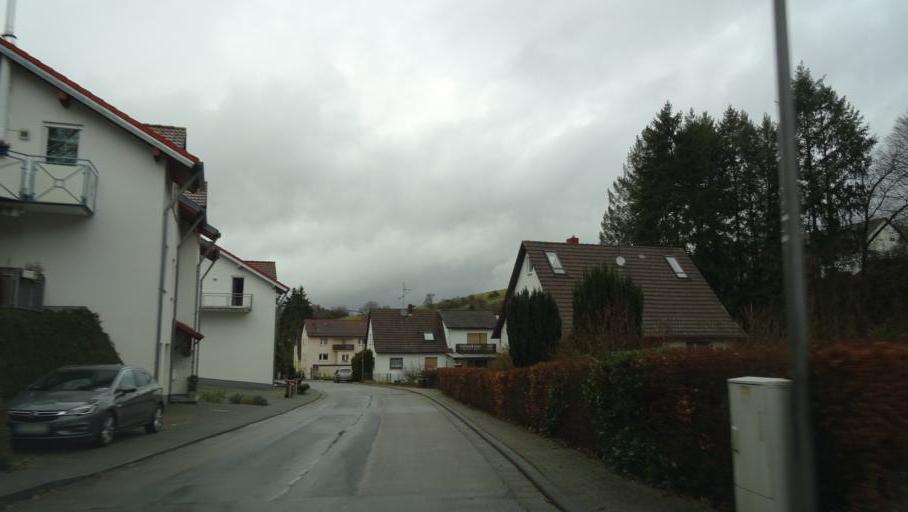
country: DE
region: Hesse
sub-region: Regierungsbezirk Darmstadt
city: Morlenbach
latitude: 49.5759
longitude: 8.7564
